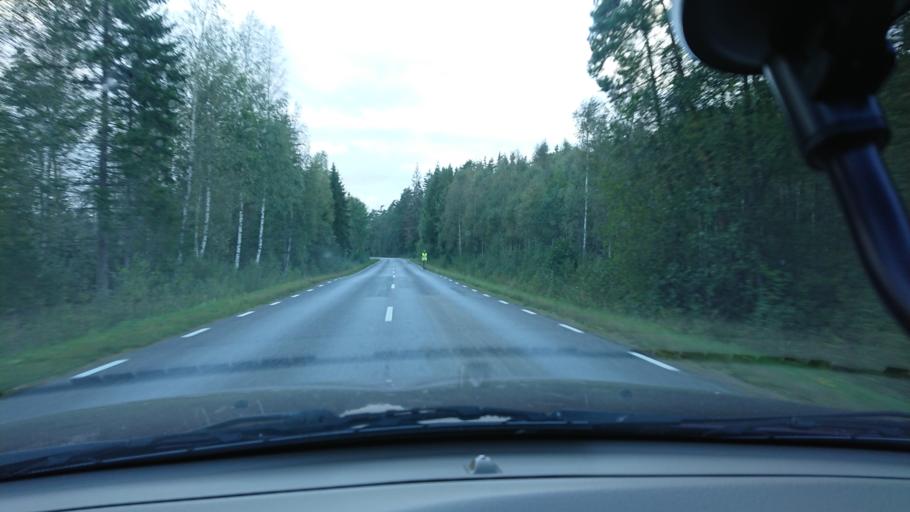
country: SE
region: Kronoberg
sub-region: Vaxjo Kommun
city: Rottne
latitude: 57.0662
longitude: 14.7434
